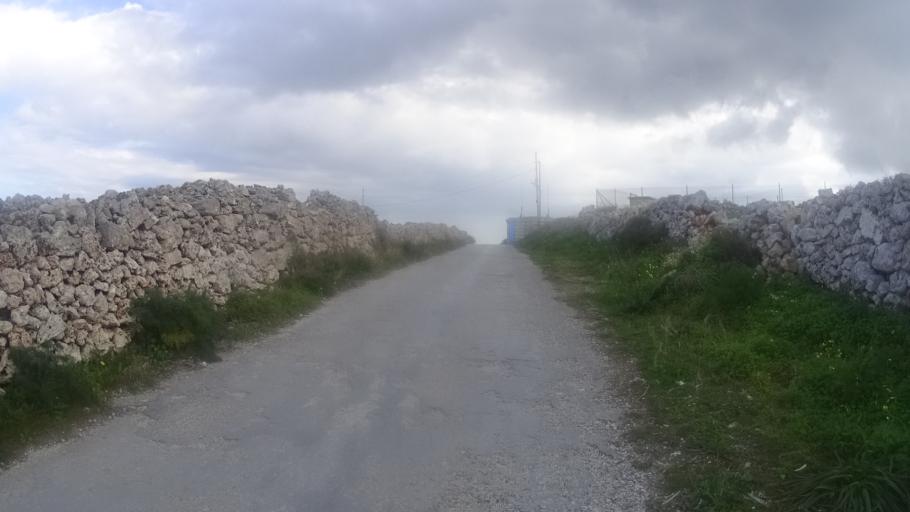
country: MT
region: L-Imgarr
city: Imgarr
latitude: 35.9011
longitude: 14.3711
